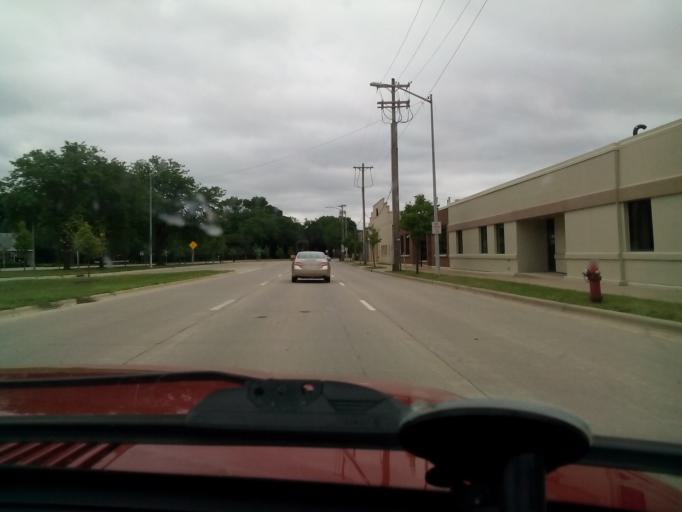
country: US
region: Wisconsin
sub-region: Dane County
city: Maple Bluff
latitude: 43.0968
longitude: -89.3604
